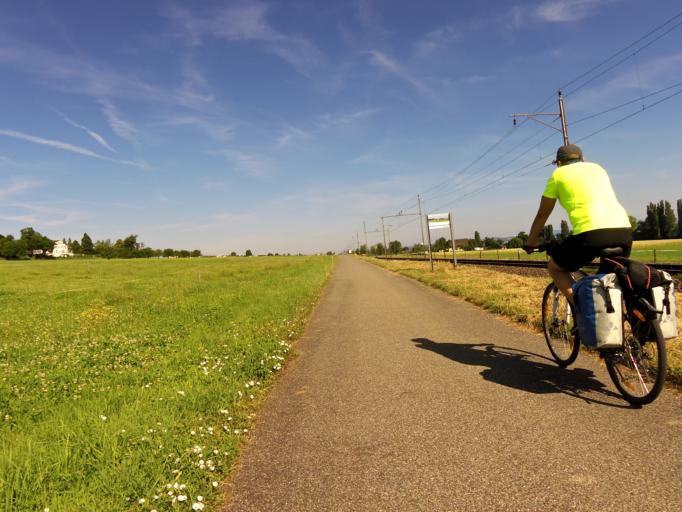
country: CH
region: Thurgau
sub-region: Kreuzlingen District
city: Guttingen
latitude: 47.6149
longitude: 9.2802
